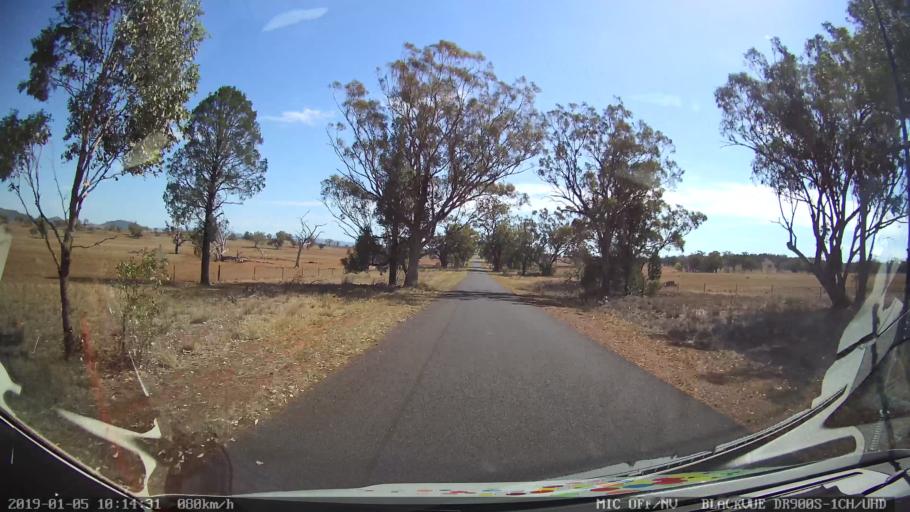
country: AU
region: New South Wales
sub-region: Gilgandra
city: Gilgandra
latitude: -31.5922
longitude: 148.9351
